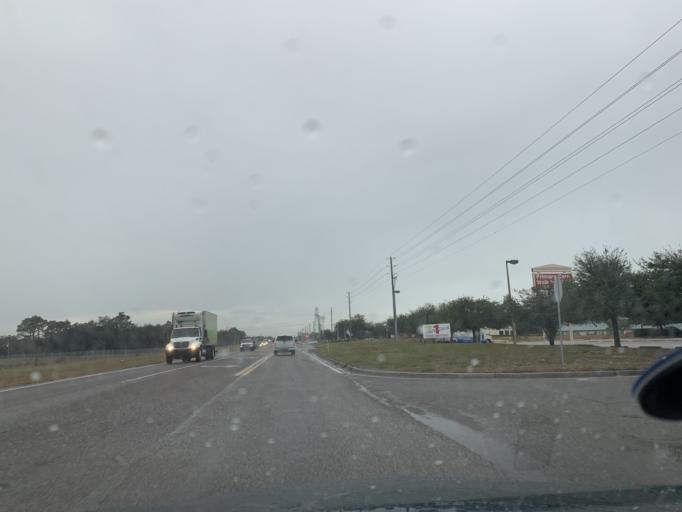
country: US
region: Florida
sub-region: Pasco County
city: Shady Hills
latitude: 28.4339
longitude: -82.5390
